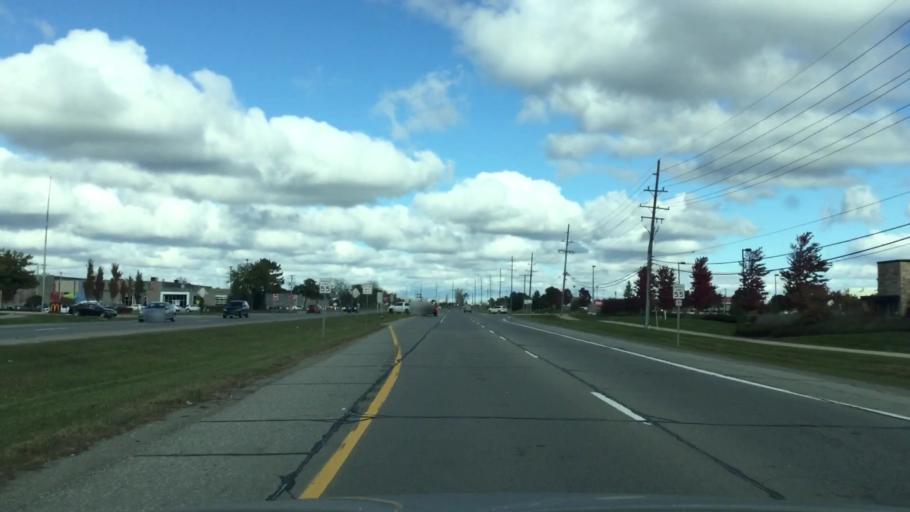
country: US
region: Michigan
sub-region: Oakland County
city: Oxford
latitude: 42.8363
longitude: -83.2720
